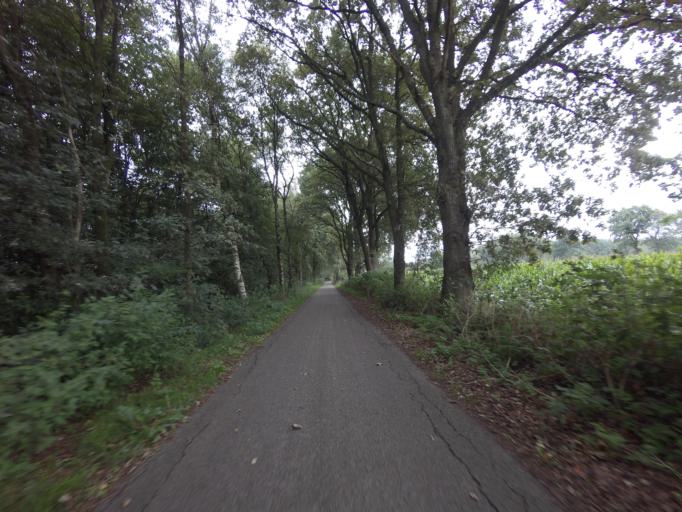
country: NL
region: Drenthe
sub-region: Gemeente Westerveld
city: Dwingeloo
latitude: 52.9060
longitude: 6.4709
